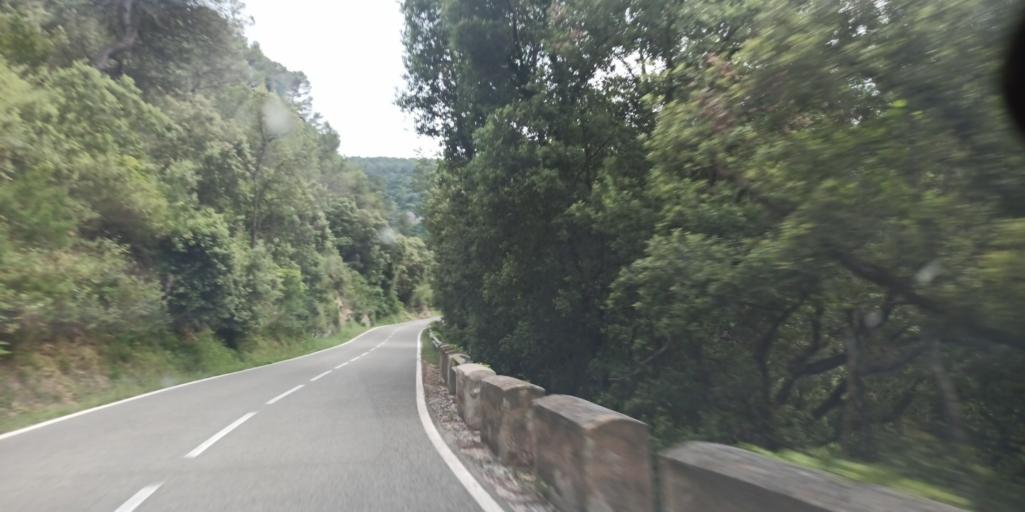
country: ES
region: Catalonia
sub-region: Provincia de Tarragona
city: Querol
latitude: 41.3899
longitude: 1.4708
